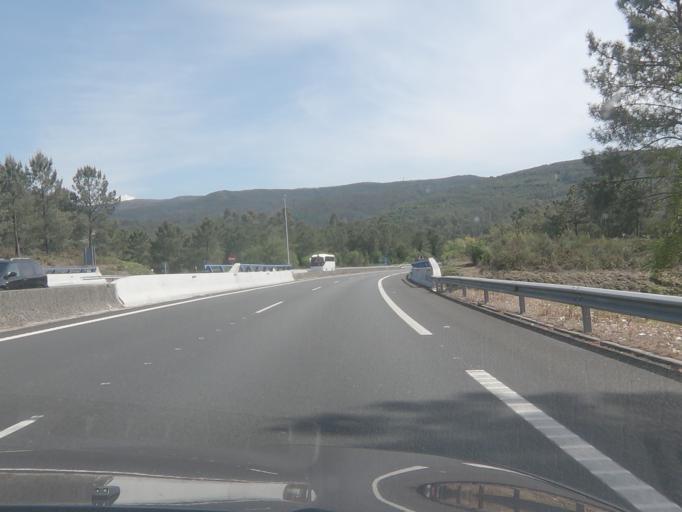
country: ES
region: Galicia
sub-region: Provincia da Coruna
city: Padron
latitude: 42.7346
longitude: -8.6384
